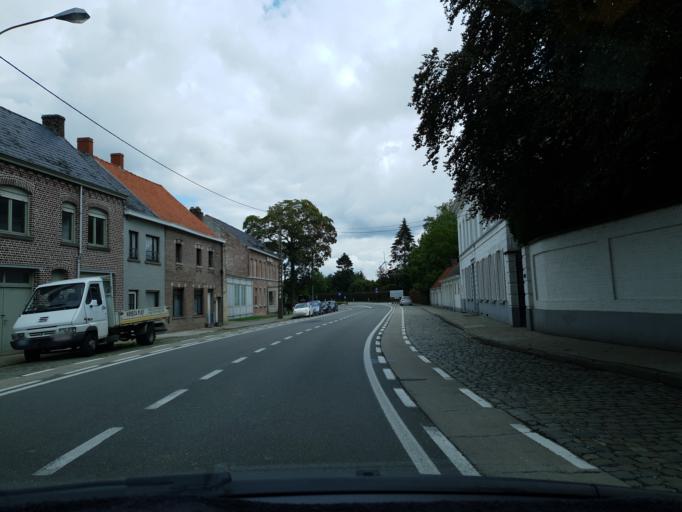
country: BE
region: Flanders
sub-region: Provincie West-Vlaanderen
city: Avelgem
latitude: 50.7567
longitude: 3.4302
